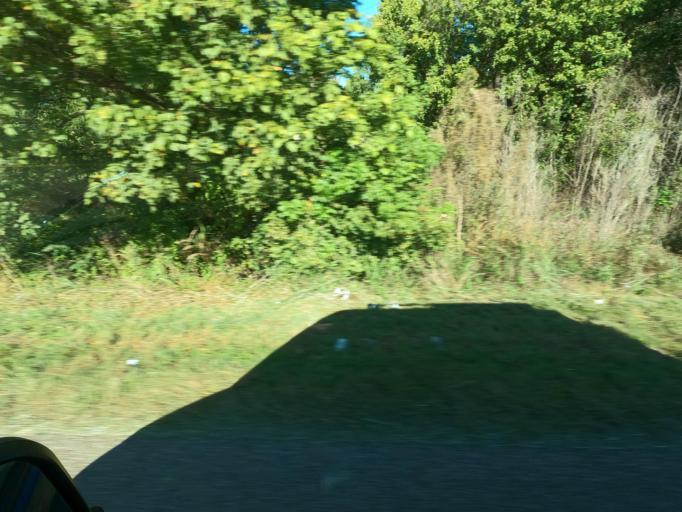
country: US
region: Tennessee
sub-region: Tipton County
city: Brighton
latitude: 35.5174
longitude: -89.7013
